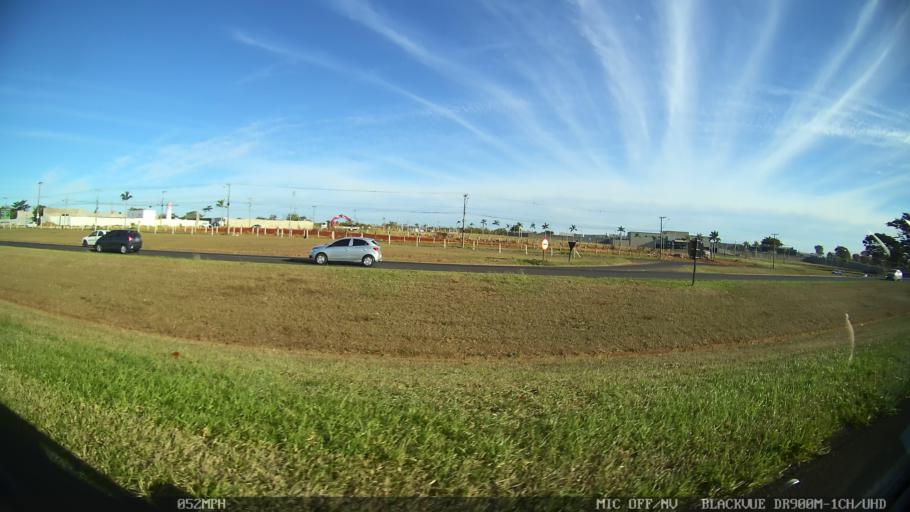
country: BR
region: Sao Paulo
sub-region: Sao Jose Do Rio Preto
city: Sao Jose do Rio Preto
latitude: -20.8234
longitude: -49.4165
